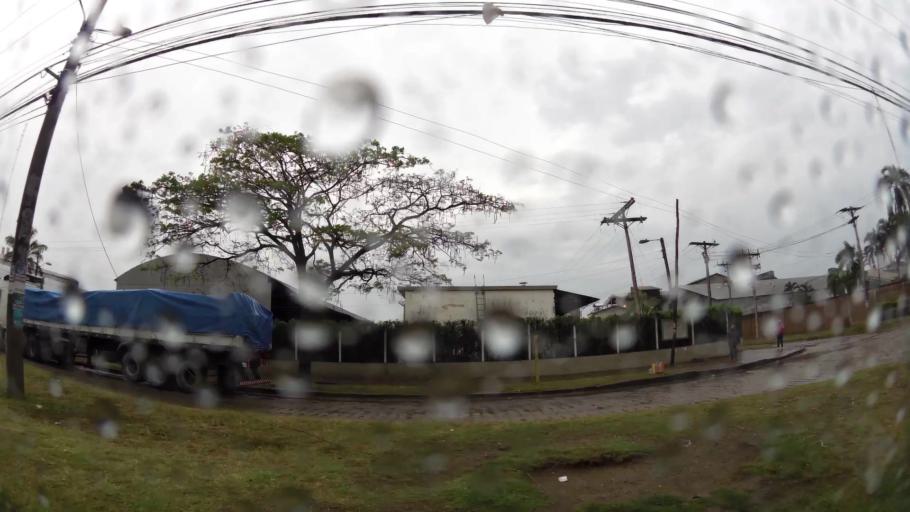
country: BO
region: Santa Cruz
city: Santa Cruz de la Sierra
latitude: -17.7706
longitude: -63.1428
